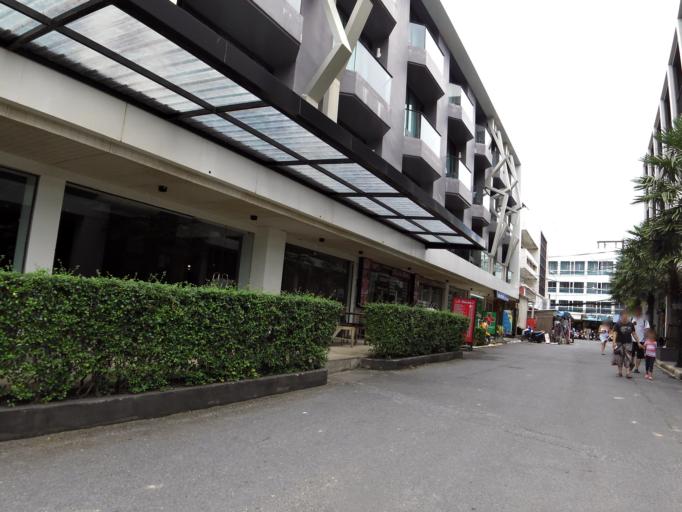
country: TH
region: Phuket
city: Ban Karon
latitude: 7.8494
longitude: 98.2941
